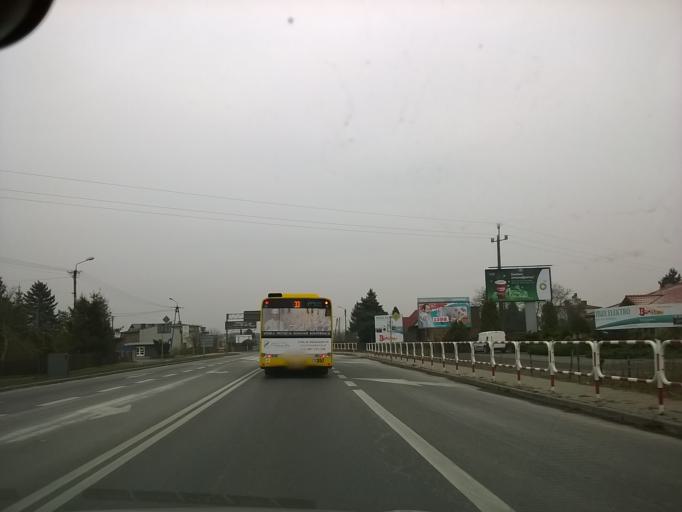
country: PL
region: Silesian Voivodeship
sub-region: Powiat gliwicki
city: Paniowki
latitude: 50.2329
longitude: 18.7902
